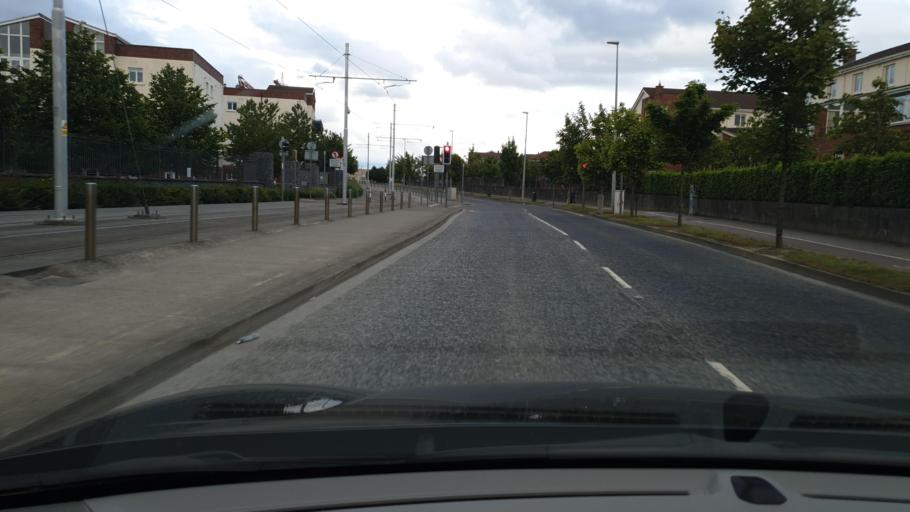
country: IE
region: Leinster
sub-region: South Dublin
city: Saggart
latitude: 53.2839
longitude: -6.4311
